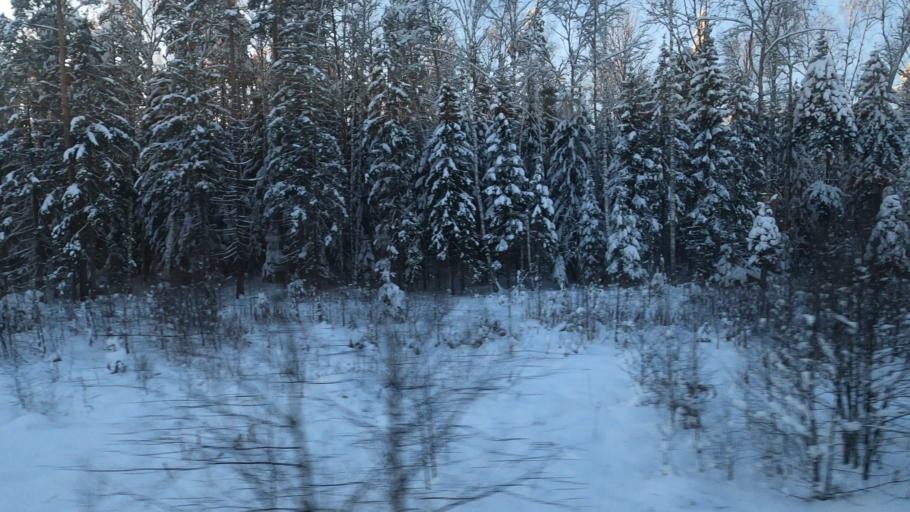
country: RU
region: Moskovskaya
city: Zhukovka
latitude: 56.5013
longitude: 37.5530
